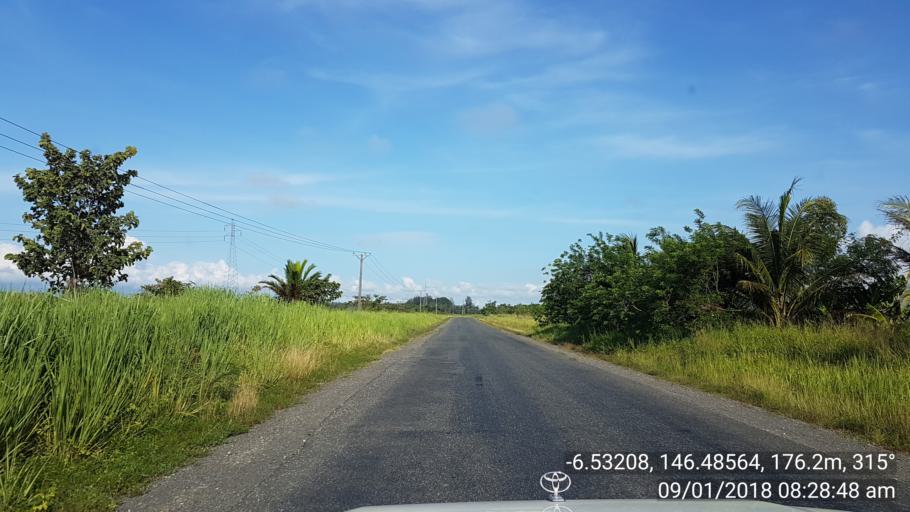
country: PG
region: Morobe
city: Lae
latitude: -6.5322
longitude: 146.4858
